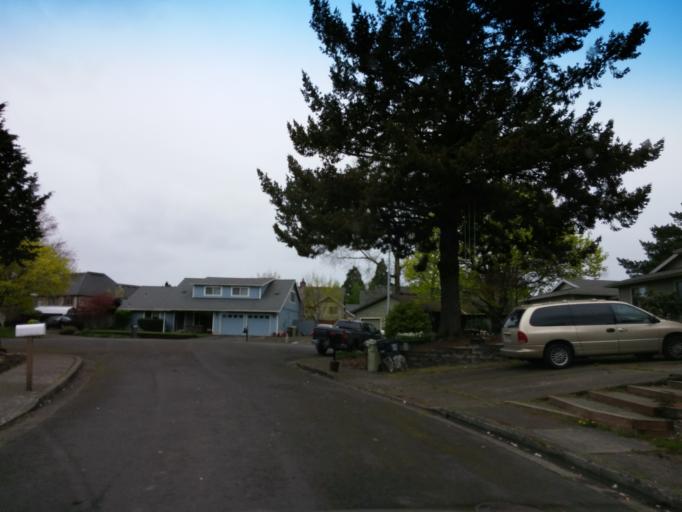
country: US
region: Oregon
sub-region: Washington County
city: Oak Hills
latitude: 45.5258
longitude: -122.8606
